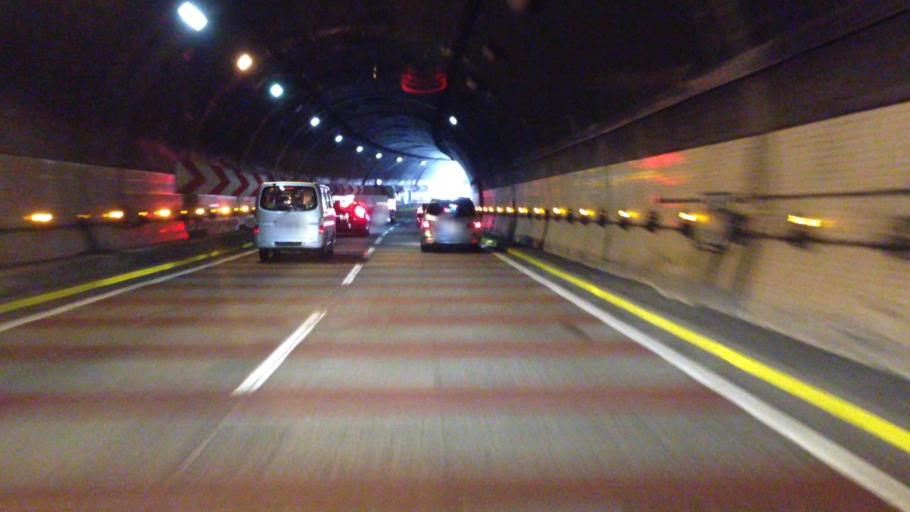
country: JP
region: Kanagawa
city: Yokohama
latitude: 35.4726
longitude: 139.5951
